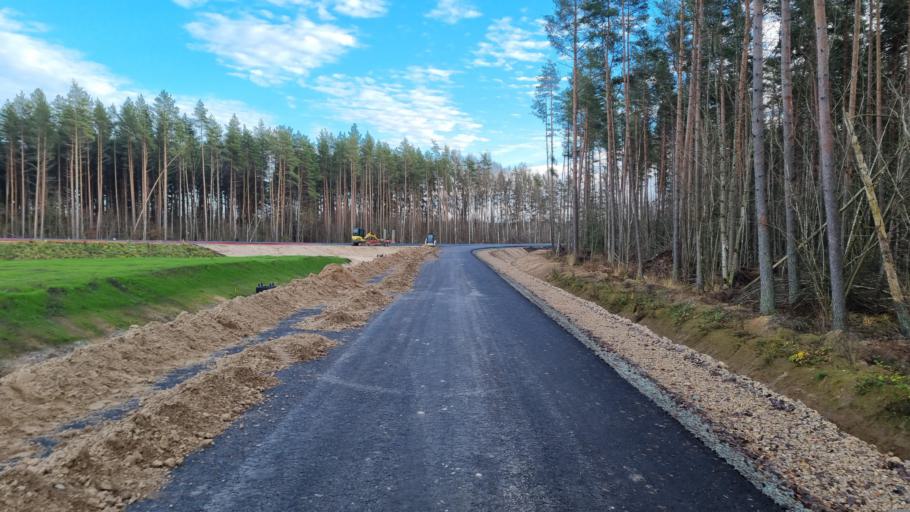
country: LV
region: Kekava
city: Kekava
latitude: 56.8066
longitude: 24.1966
